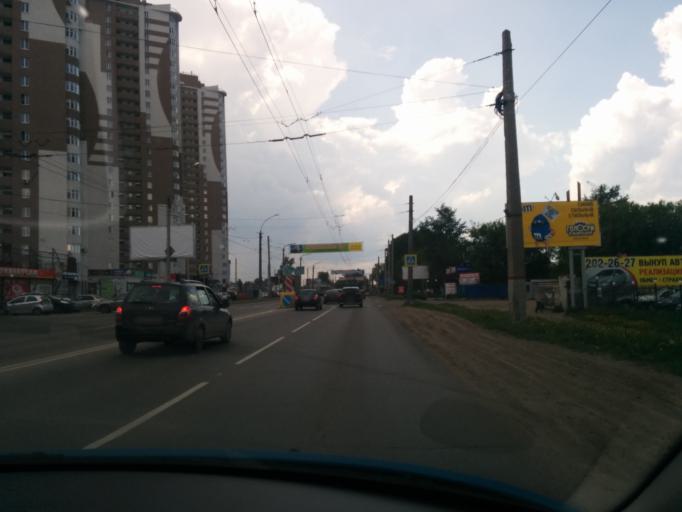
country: RU
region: Perm
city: Kondratovo
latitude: 57.9714
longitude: 56.1544
